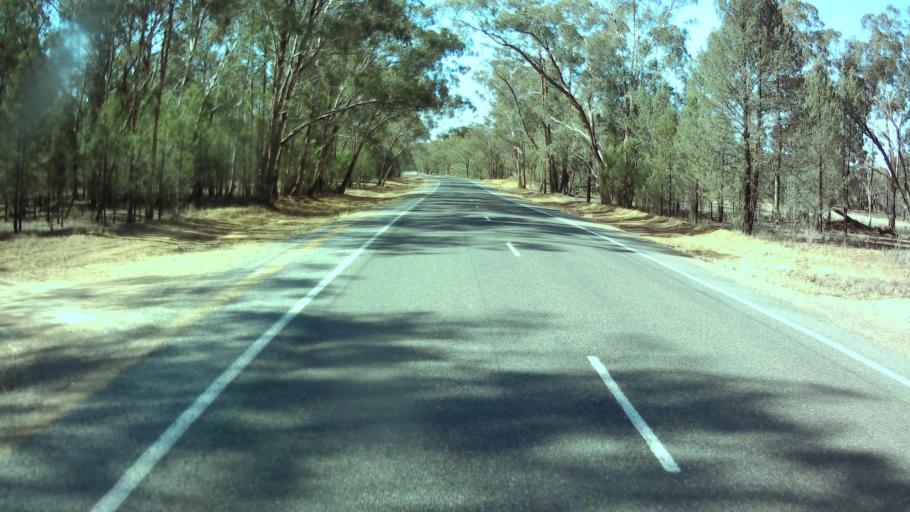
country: AU
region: New South Wales
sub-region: Weddin
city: Grenfell
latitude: -33.7603
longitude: 148.0823
